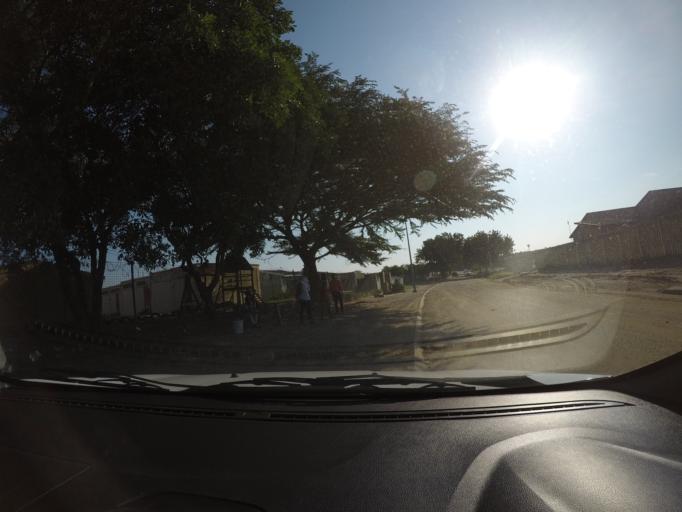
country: ZA
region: KwaZulu-Natal
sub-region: uThungulu District Municipality
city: Richards Bay
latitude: -28.7138
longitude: 32.0338
